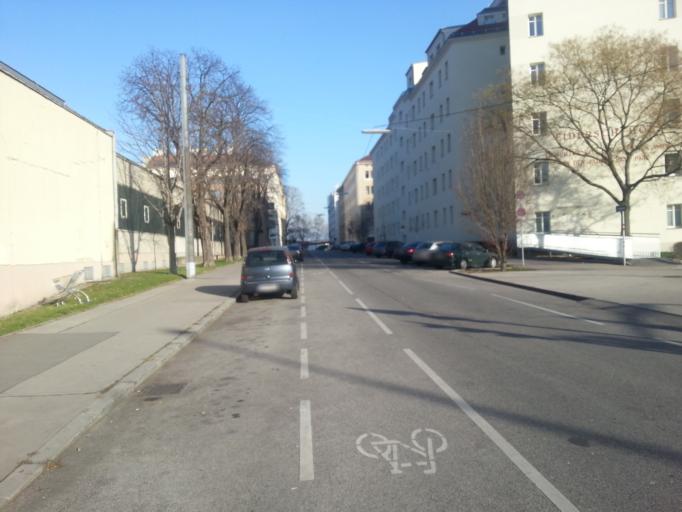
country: AT
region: Vienna
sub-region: Wien Stadt
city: Vienna
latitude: 48.2180
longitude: 16.4099
